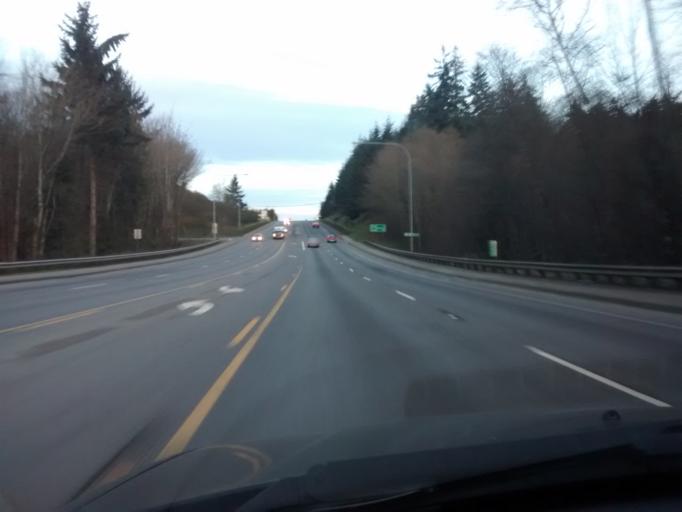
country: US
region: Washington
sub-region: Clallam County
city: Port Angeles East
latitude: 48.1057
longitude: -123.3950
